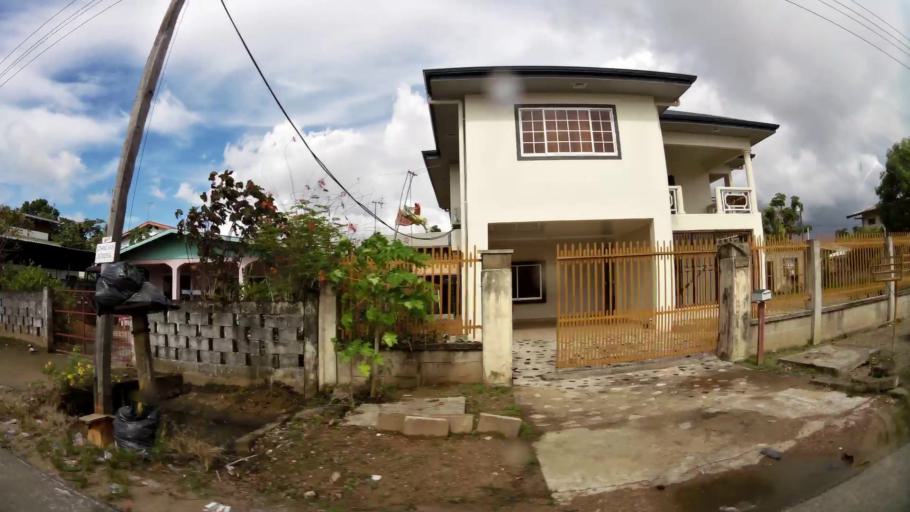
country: SR
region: Paramaribo
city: Paramaribo
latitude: 5.8434
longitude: -55.2049
